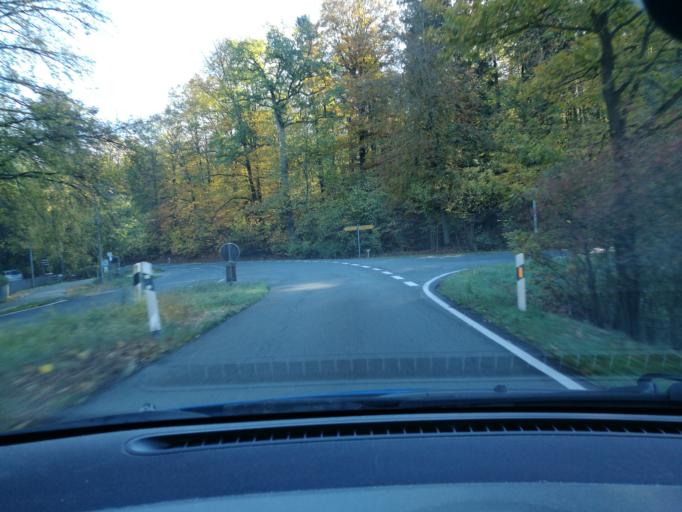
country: DE
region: Lower Saxony
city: Gohrde
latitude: 53.1391
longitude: 10.8791
